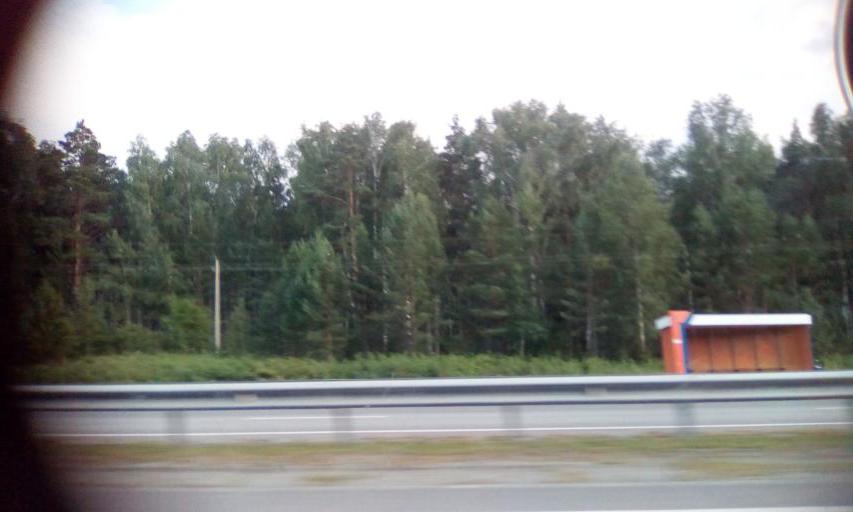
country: RU
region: Chelyabinsk
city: Sargazy
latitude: 55.0114
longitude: 61.2623
